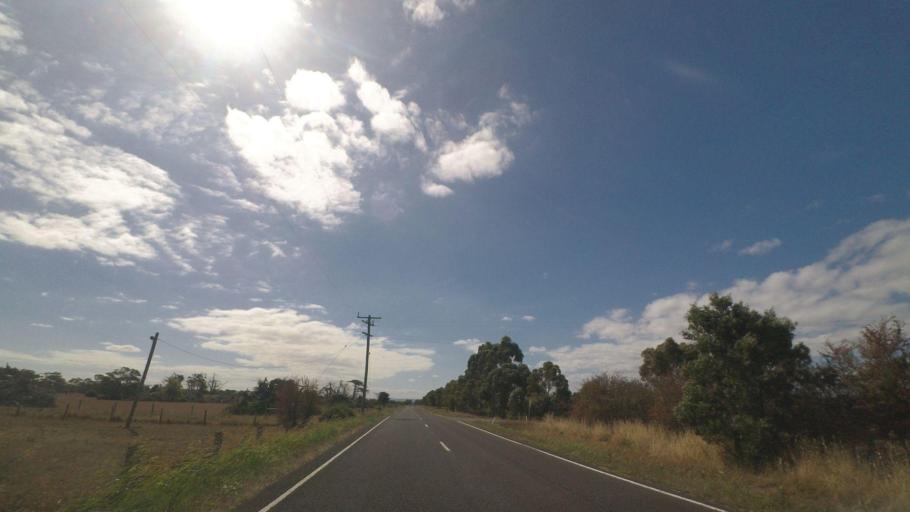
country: AU
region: Victoria
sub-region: Cardinia
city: Garfield
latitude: -38.1969
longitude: 145.6267
